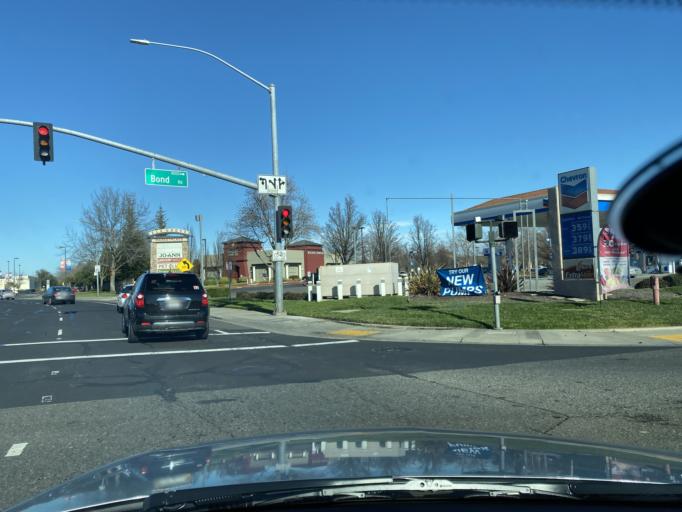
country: US
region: California
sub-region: Sacramento County
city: Elk Grove
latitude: 38.4237
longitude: -121.3901
